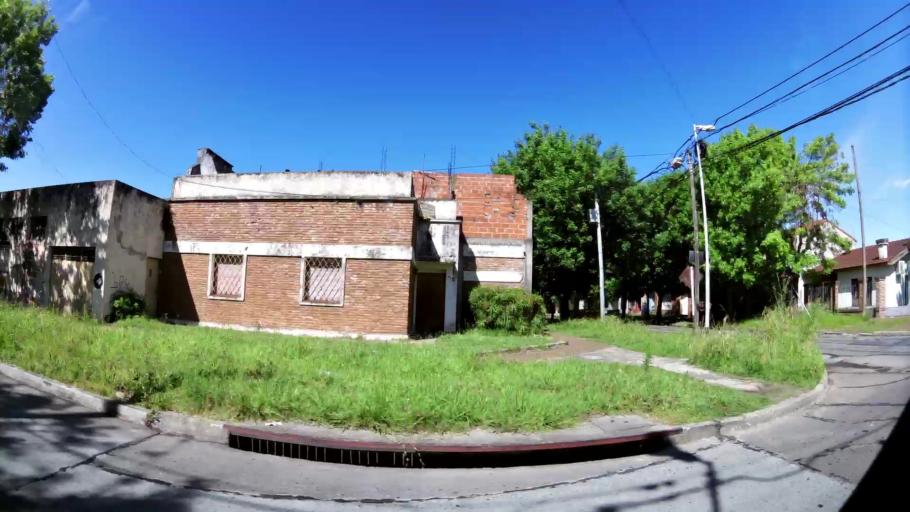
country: AR
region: Buenos Aires
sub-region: Partido de Quilmes
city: Quilmes
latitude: -34.6949
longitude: -58.3026
